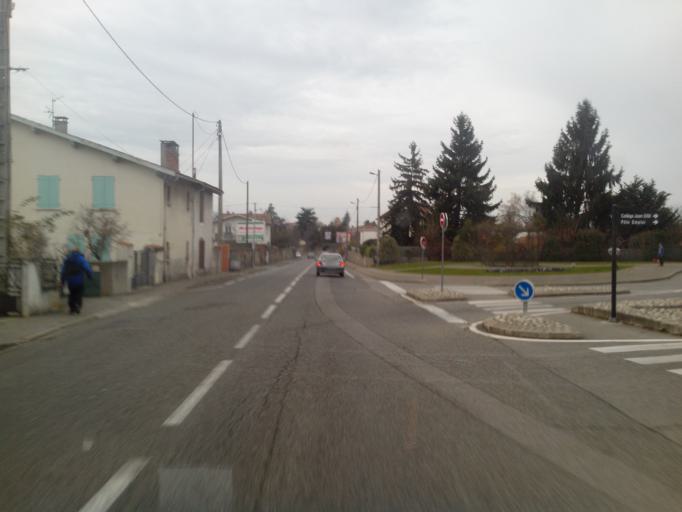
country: FR
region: Midi-Pyrenees
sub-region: Departement de l'Ariege
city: Pamiers
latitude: 43.1077
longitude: 1.6178
